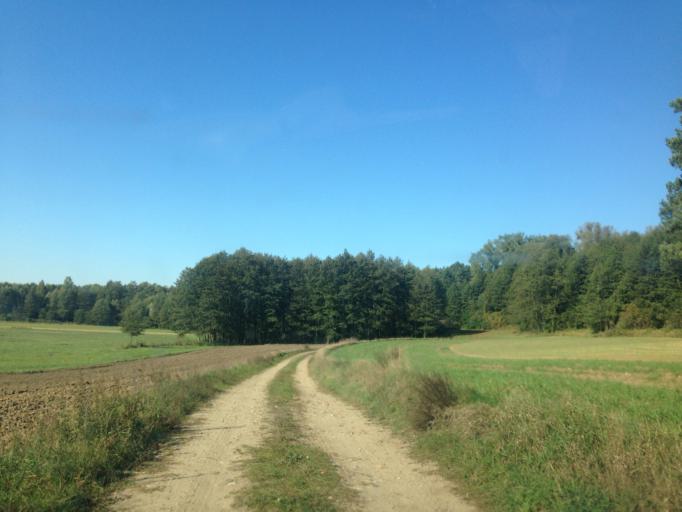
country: PL
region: Kujawsko-Pomorskie
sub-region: Powiat brodnicki
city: Bartniczka
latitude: 53.2759
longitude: 19.6245
